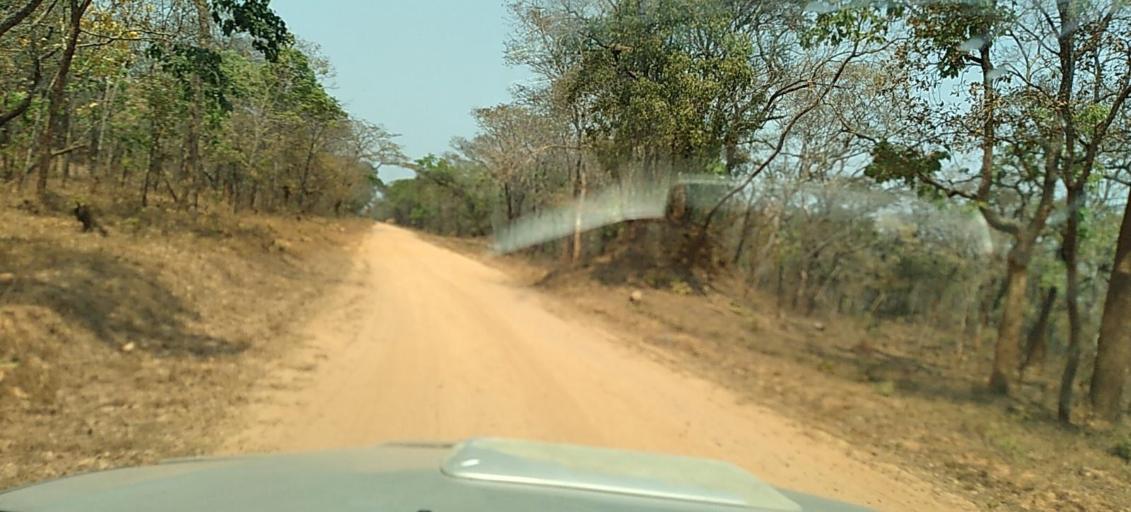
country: ZM
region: North-Western
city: Kasempa
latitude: -13.6600
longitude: 26.2685
